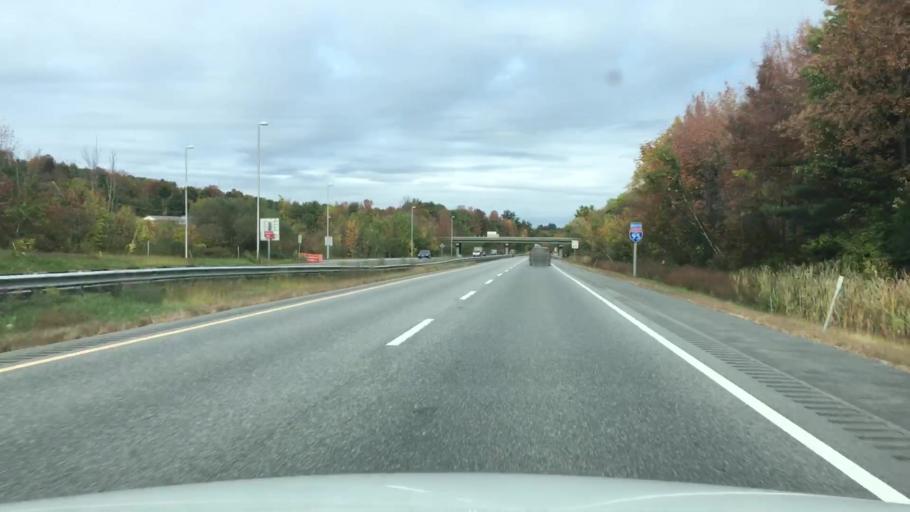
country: US
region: Maine
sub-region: Kennebec County
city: Augusta
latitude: 44.3177
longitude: -69.8121
